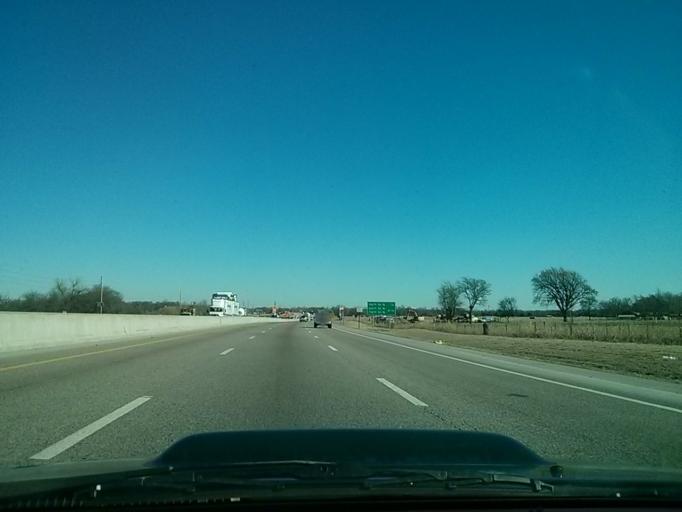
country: US
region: Oklahoma
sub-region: Tulsa County
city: Owasso
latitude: 36.2268
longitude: -95.8509
